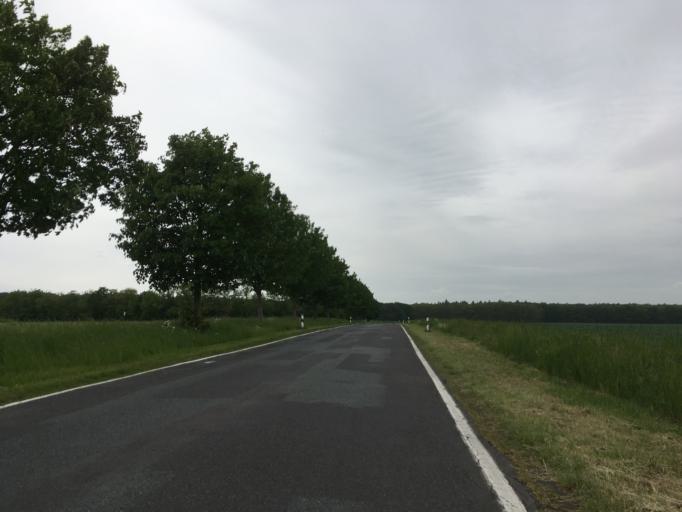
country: DE
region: Brandenburg
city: Werftpfuhl
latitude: 52.7369
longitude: 13.8238
